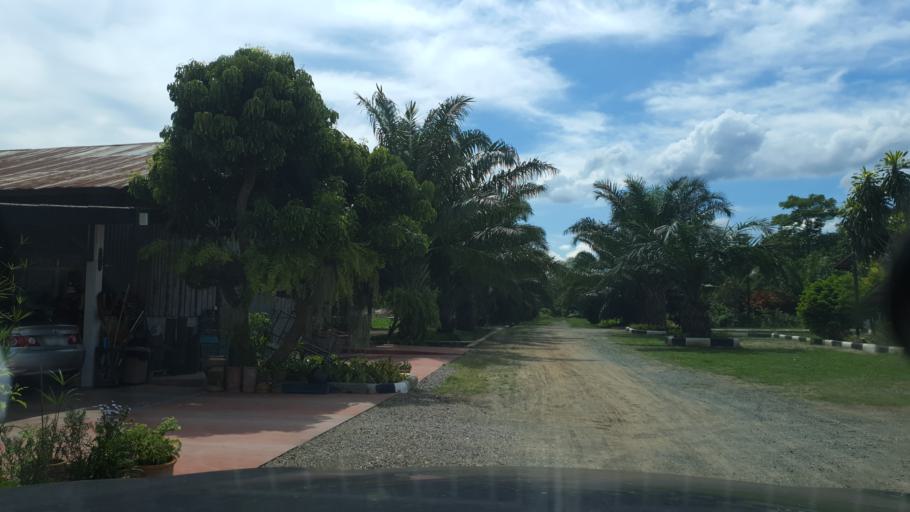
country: TH
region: Chiang Mai
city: San Sai
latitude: 18.9089
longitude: 98.9469
